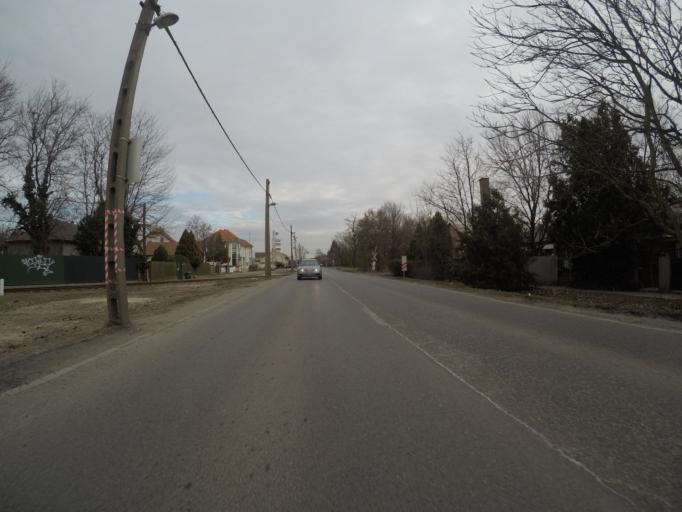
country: HU
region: Budapest
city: Budapest X. keruelet
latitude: 47.4945
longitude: 19.1621
